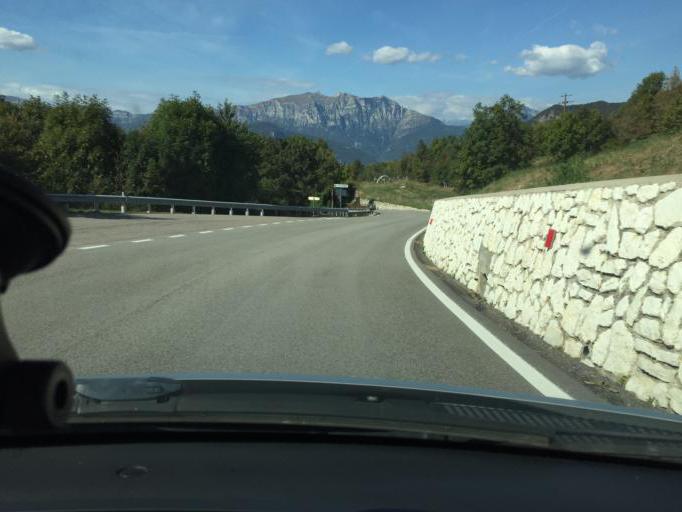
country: IT
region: Trentino-Alto Adige
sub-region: Provincia di Trento
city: Folgaria
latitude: 45.9130
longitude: 11.1541
